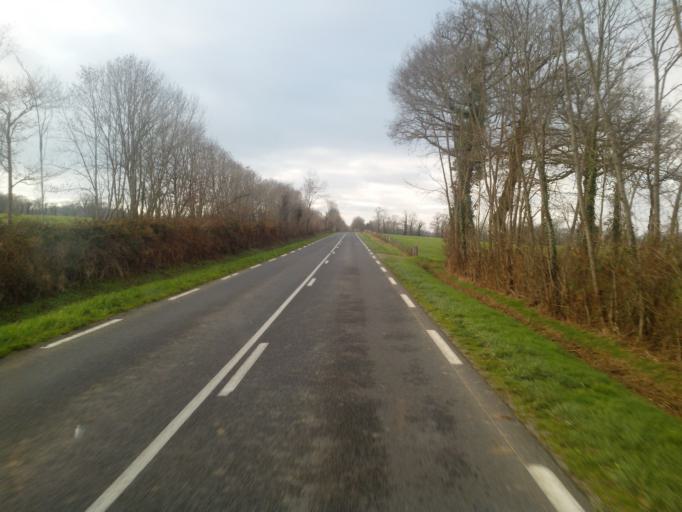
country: FR
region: Limousin
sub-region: Departement de la Haute-Vienne
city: Le Dorat
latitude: 46.2147
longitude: 1.1102
